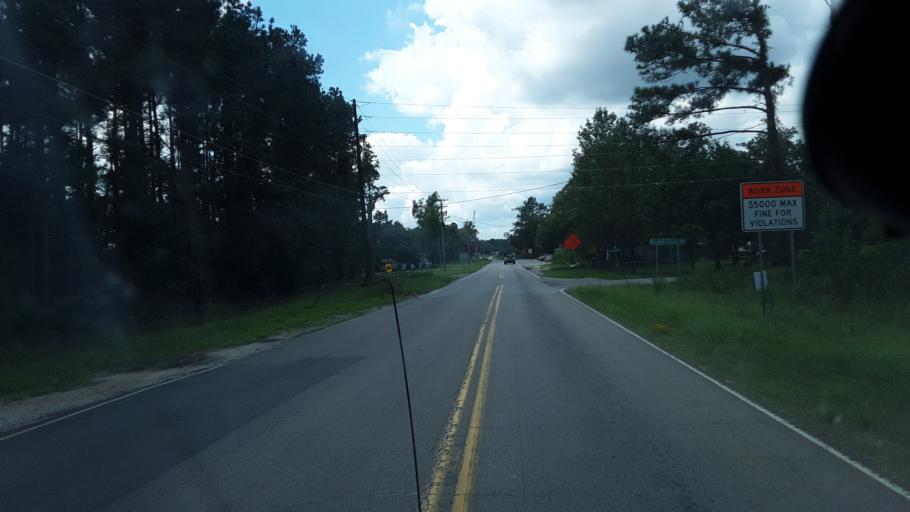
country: US
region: South Carolina
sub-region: Williamsburg County
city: Andrews
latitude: 33.3745
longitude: -79.4461
